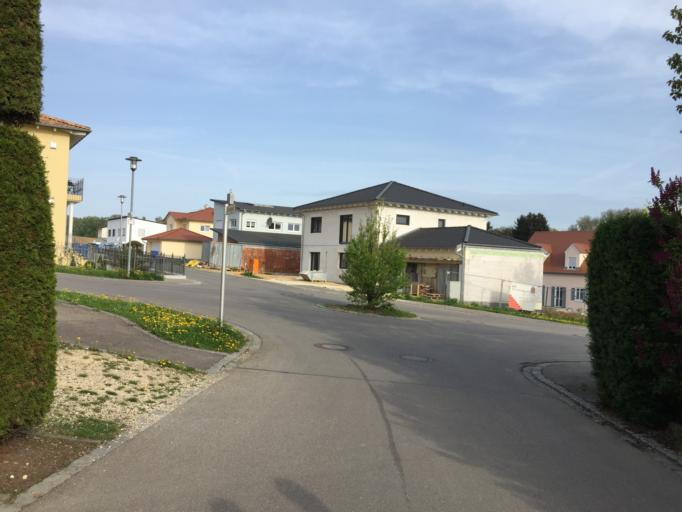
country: DE
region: Bavaria
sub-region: Swabia
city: Wertingen
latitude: 48.5690
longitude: 10.6758
